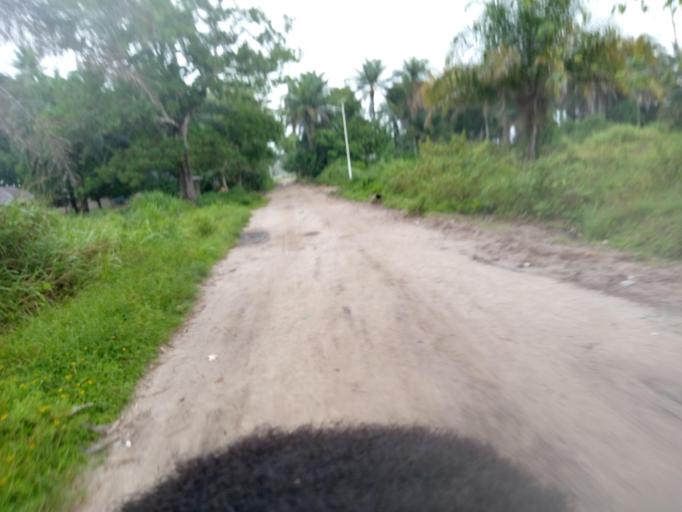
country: SL
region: Southern Province
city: Bonthe
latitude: 7.5278
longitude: -12.5100
